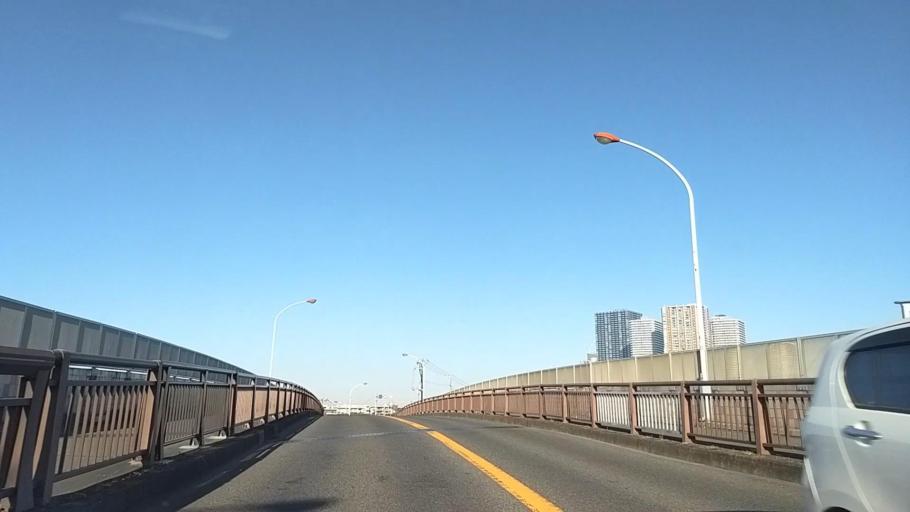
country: JP
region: Kanagawa
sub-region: Kawasaki-shi
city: Kawasaki
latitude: 35.5640
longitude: 139.6670
